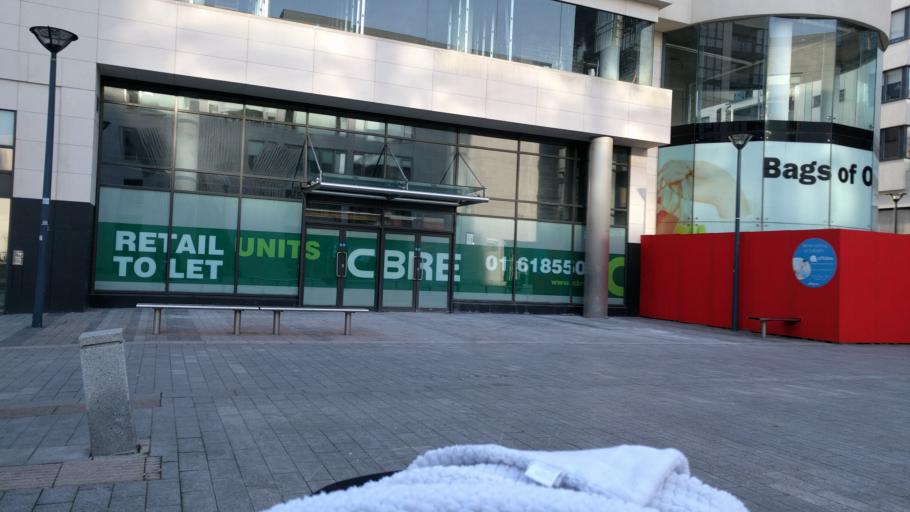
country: IE
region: Leinster
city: Tallaght
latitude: 53.2882
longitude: -6.3740
